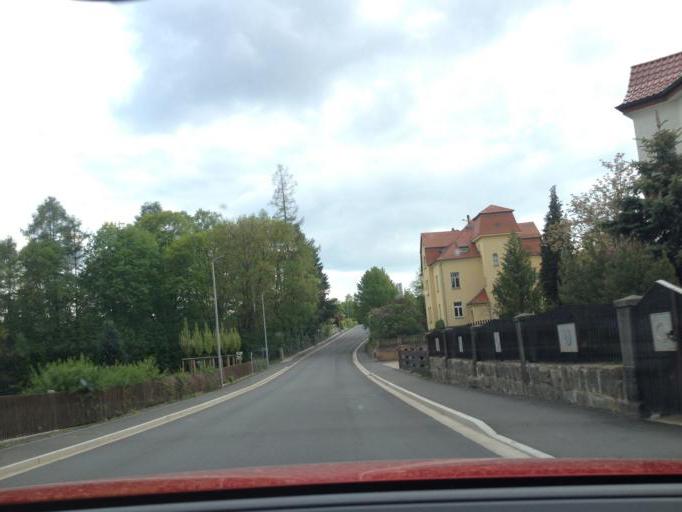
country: DE
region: Bavaria
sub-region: Upper Franconia
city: Arzberg
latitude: 50.0551
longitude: 12.1810
